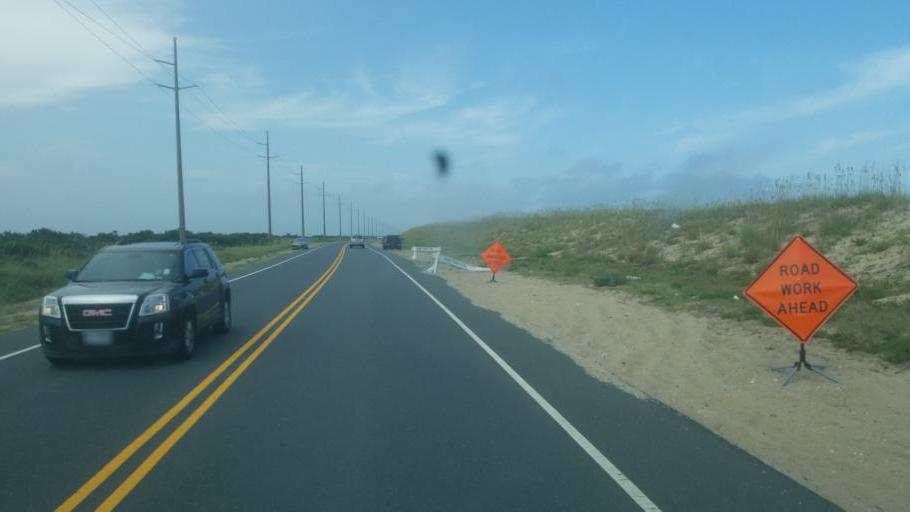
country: US
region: North Carolina
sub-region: Dare County
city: Buxton
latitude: 35.2692
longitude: -75.5187
